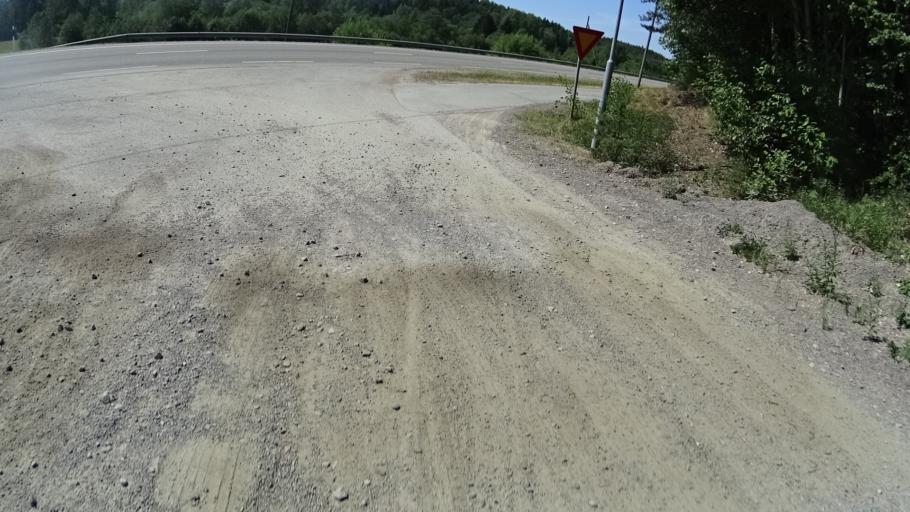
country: FI
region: Uusimaa
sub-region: Raaseporin
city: Karis
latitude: 60.0956
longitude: 23.6158
